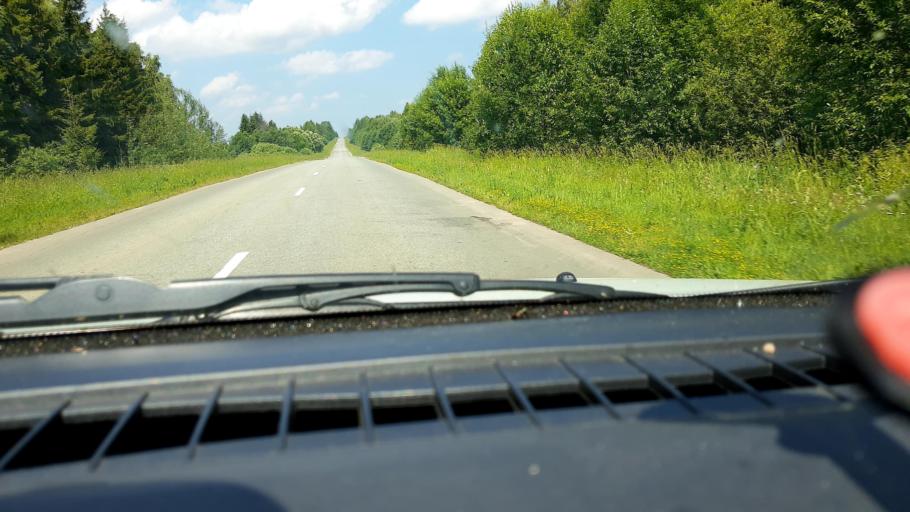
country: RU
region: Nizjnij Novgorod
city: Sharanga
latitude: 57.0905
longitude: 46.5340
